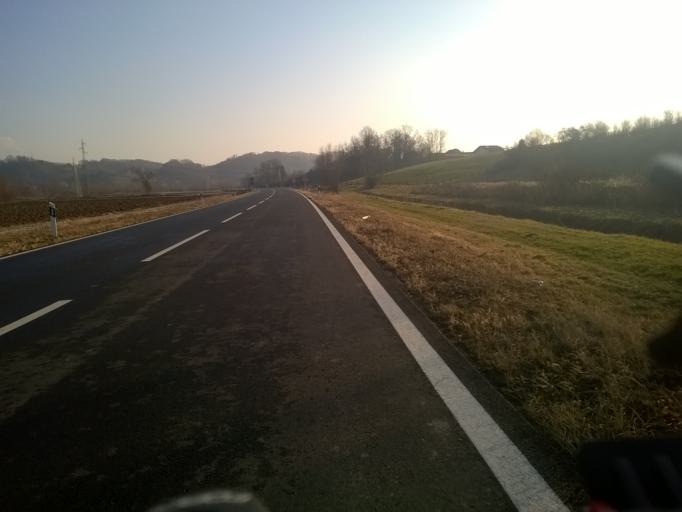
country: HR
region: Krapinsko-Zagorska
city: Zabok
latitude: 46.0399
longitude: 15.9167
